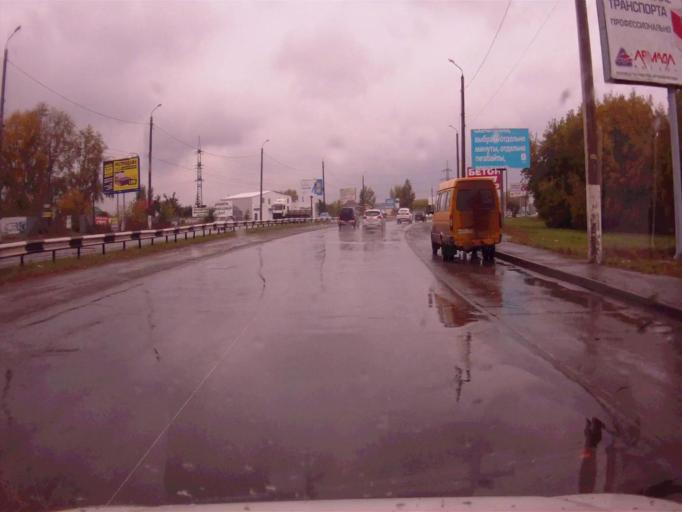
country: RU
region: Chelyabinsk
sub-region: Gorod Chelyabinsk
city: Chelyabinsk
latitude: 55.2373
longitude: 61.3620
